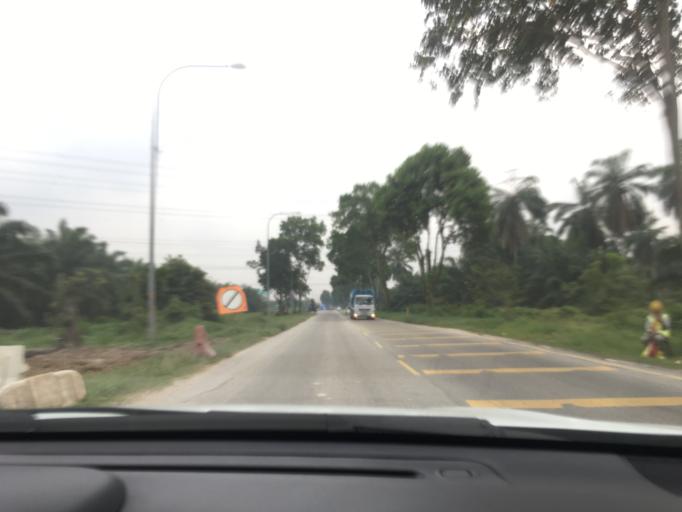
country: MY
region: Selangor
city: Klang
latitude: 3.1362
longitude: 101.4009
